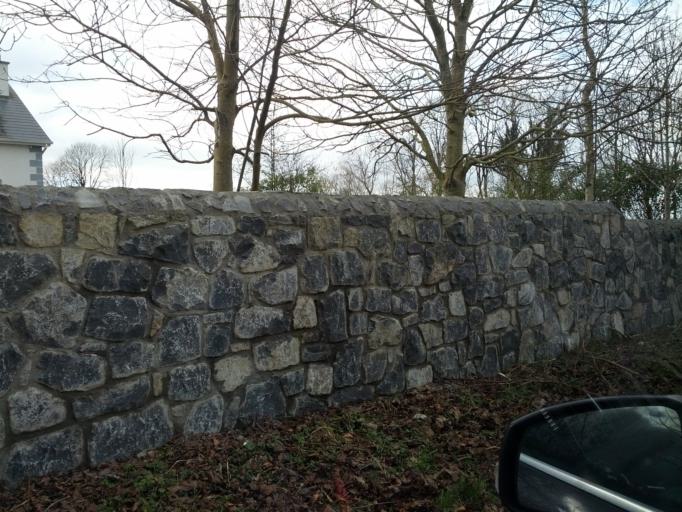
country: IE
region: Connaught
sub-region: County Galway
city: Athenry
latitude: 53.3838
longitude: -8.6587
